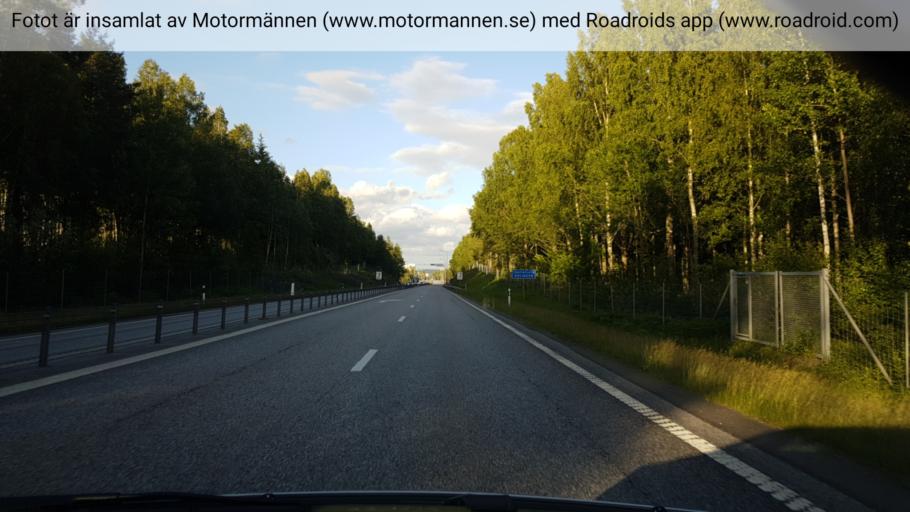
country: SE
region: OErebro
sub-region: Karlskoga Kommun
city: Karlskoga
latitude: 59.3249
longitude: 14.4478
